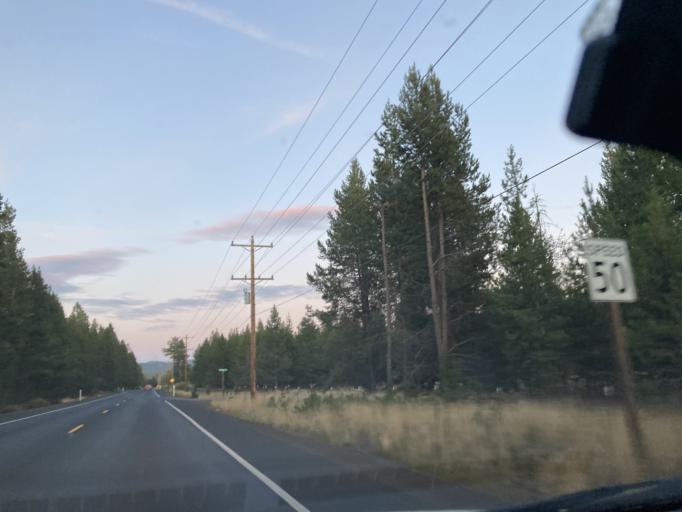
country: US
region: Oregon
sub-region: Deschutes County
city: Three Rivers
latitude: 43.8194
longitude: -121.4622
